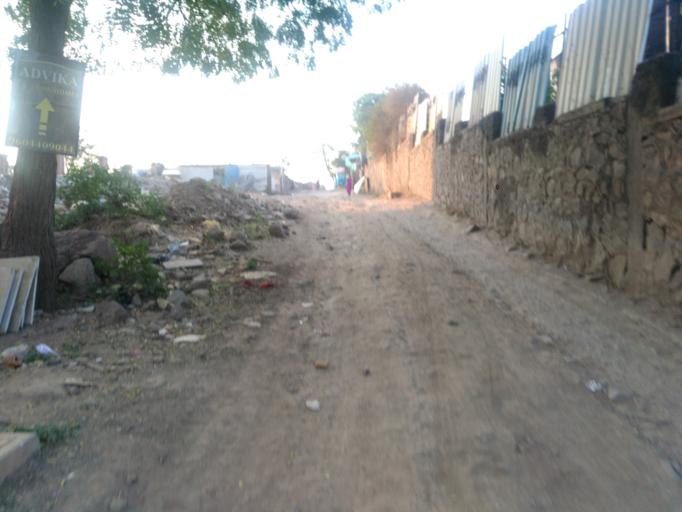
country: IN
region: Maharashtra
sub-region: Pune Division
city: Pune
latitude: 18.4455
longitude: 73.8979
